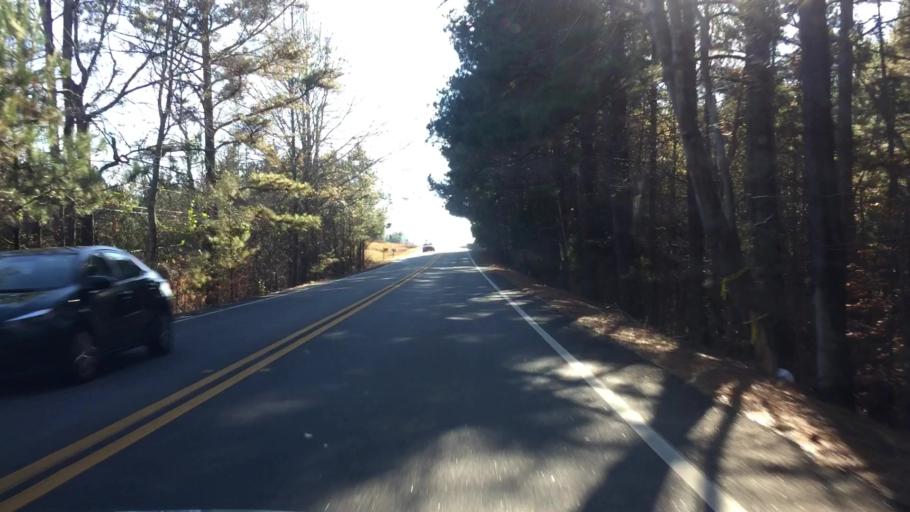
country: US
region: Georgia
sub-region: Newton County
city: Oakwood
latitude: 33.4715
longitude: -83.9646
